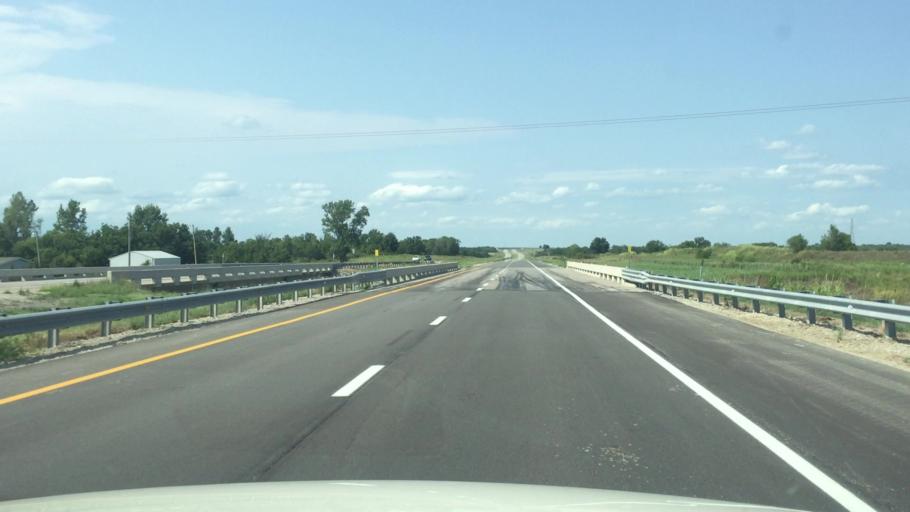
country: US
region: Kansas
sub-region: Linn County
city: La Cygne
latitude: 38.3738
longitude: -94.6874
